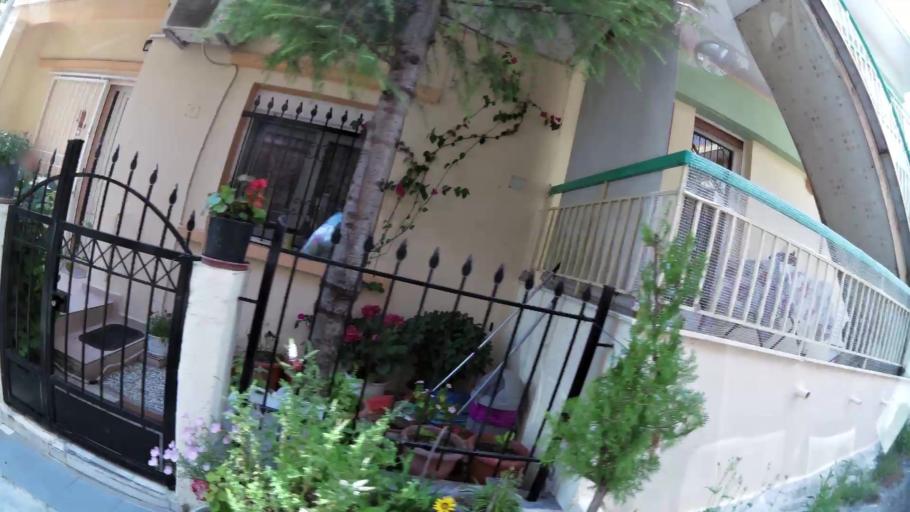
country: GR
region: Central Macedonia
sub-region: Nomos Thessalonikis
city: Polichni
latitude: 40.6635
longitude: 22.9535
